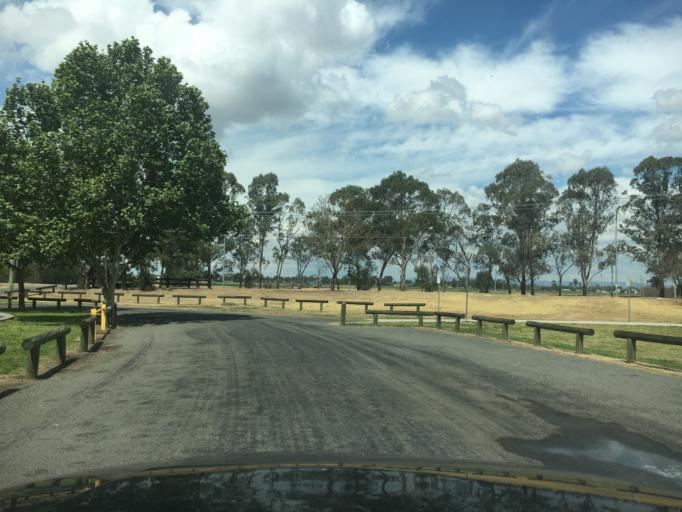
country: AU
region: New South Wales
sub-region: Singleton
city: Singleton
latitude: -32.5473
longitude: 151.1690
